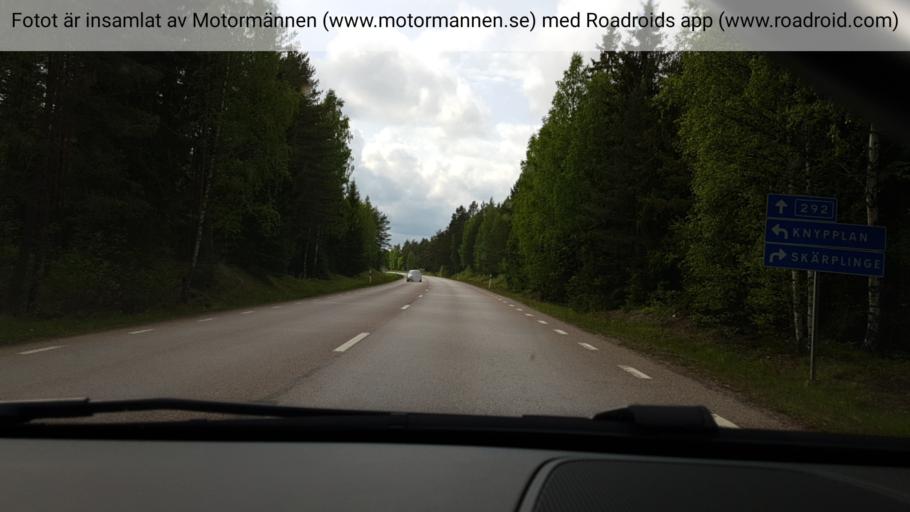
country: SE
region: Uppsala
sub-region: Tierps Kommun
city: Orbyhus
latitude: 60.2160
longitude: 17.7449
